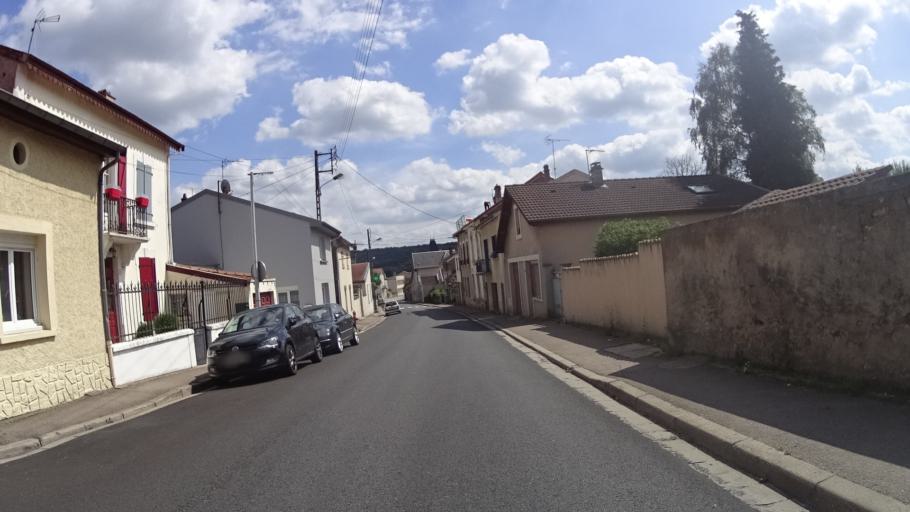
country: FR
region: Lorraine
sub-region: Departement de Meurthe-et-Moselle
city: Foug
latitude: 48.6832
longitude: 5.7892
